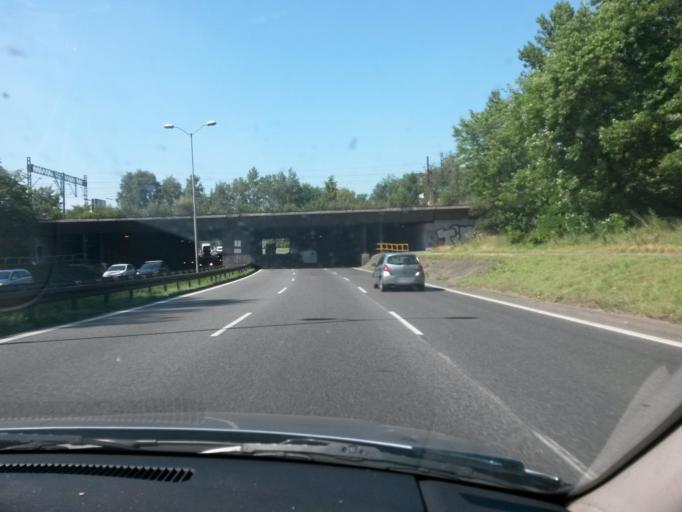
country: PL
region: Silesian Voivodeship
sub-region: Katowice
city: Katowice
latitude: 50.2569
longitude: 19.0484
